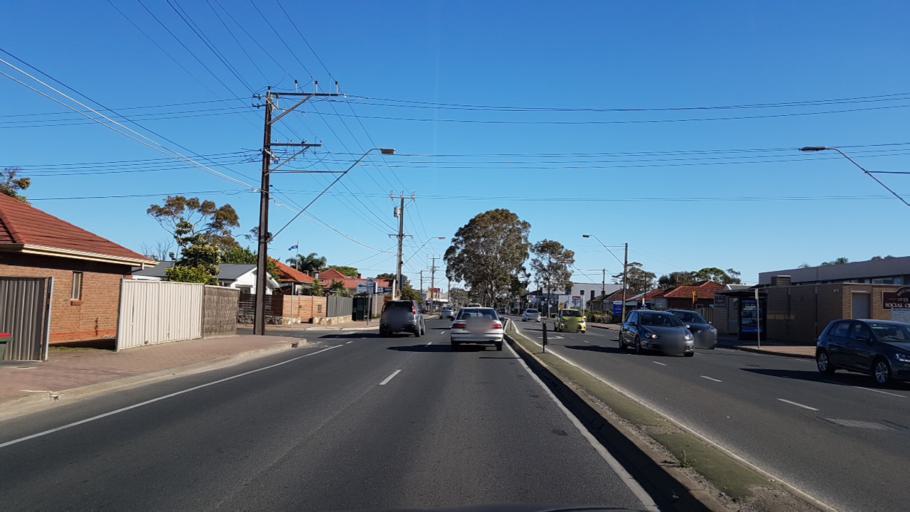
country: AU
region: South Australia
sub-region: Adelaide
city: Brighton
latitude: -35.0117
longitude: 138.5225
